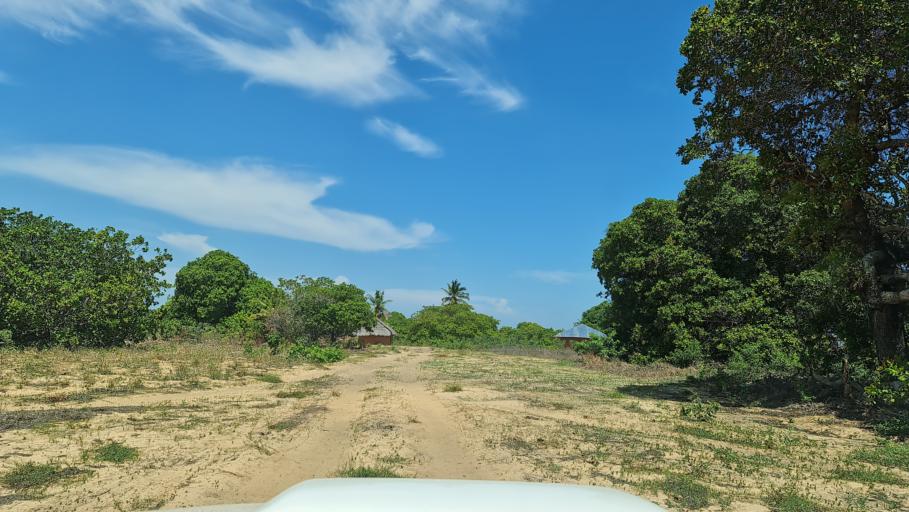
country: MZ
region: Nampula
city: Ilha de Mocambique
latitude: -15.1983
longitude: 40.6114
